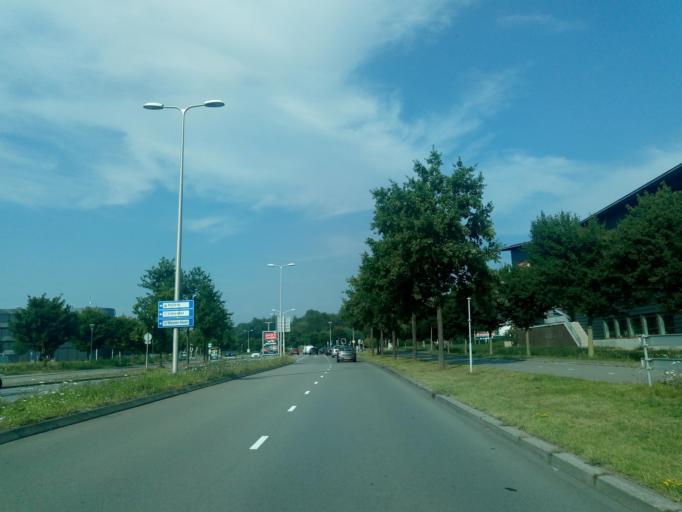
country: NL
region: South Holland
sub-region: Gemeente Alphen aan den Rijn
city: Alphen aan den Rijn
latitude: 52.1362
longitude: 4.6707
